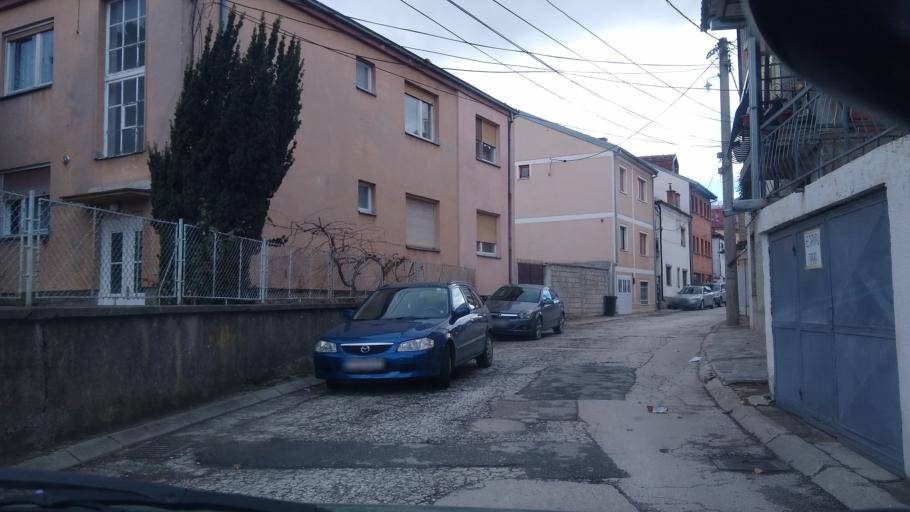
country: MK
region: Bitola
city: Bitola
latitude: 41.0246
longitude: 21.3315
